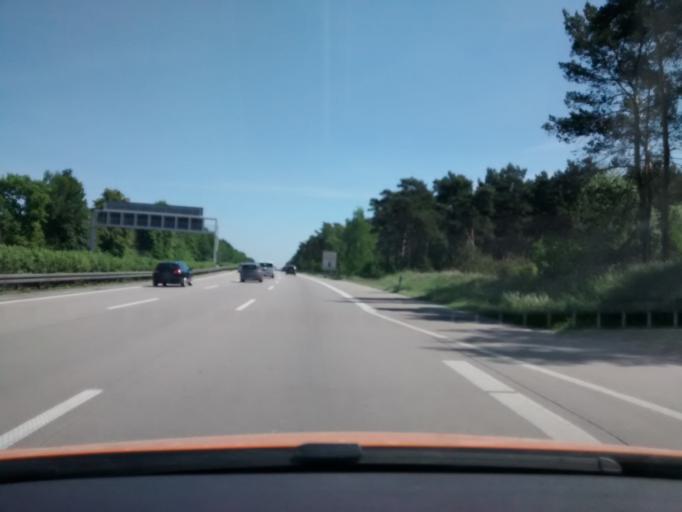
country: DE
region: Brandenburg
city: Wildau
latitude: 52.3140
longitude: 13.6699
